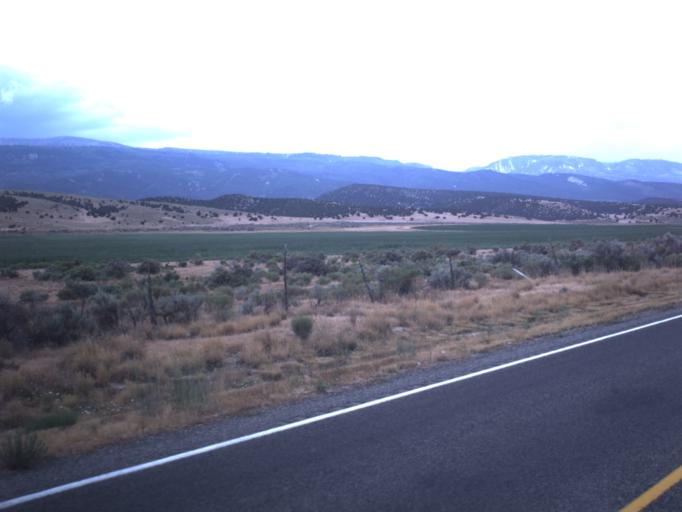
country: US
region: Utah
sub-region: Sanpete County
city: Ephraim
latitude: 39.4391
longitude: -111.5624
